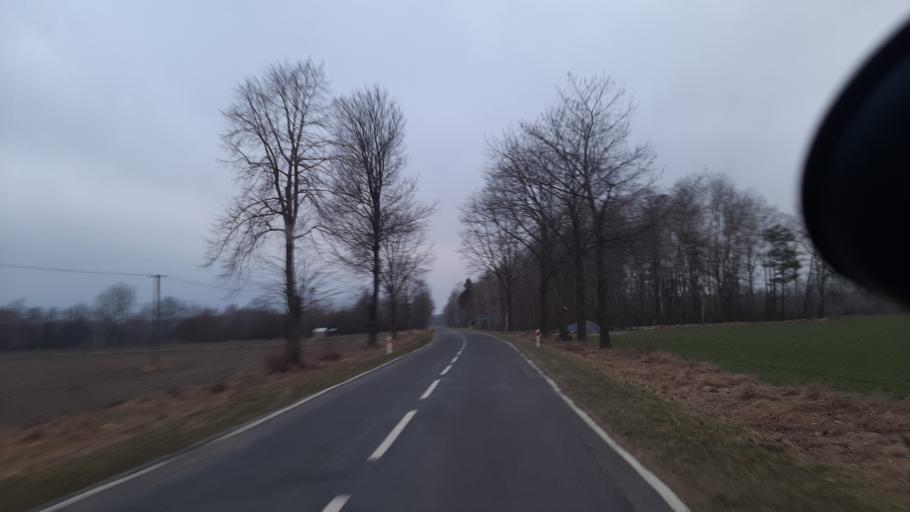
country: PL
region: Lublin Voivodeship
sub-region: Powiat parczewski
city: Podedworze
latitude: 51.5958
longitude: 23.1625
